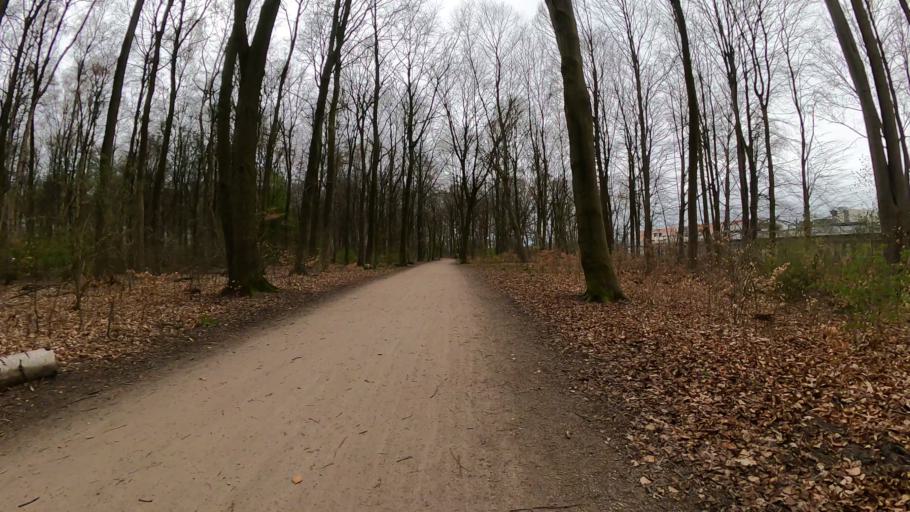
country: DE
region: Hamburg
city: Winterhude
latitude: 53.6192
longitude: 9.9889
